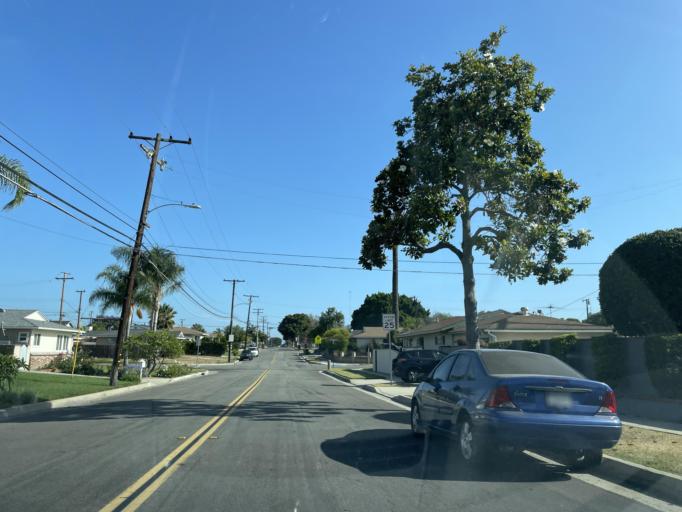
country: US
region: California
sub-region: Los Angeles County
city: La Mirada
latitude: 33.8957
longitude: -118.0117
